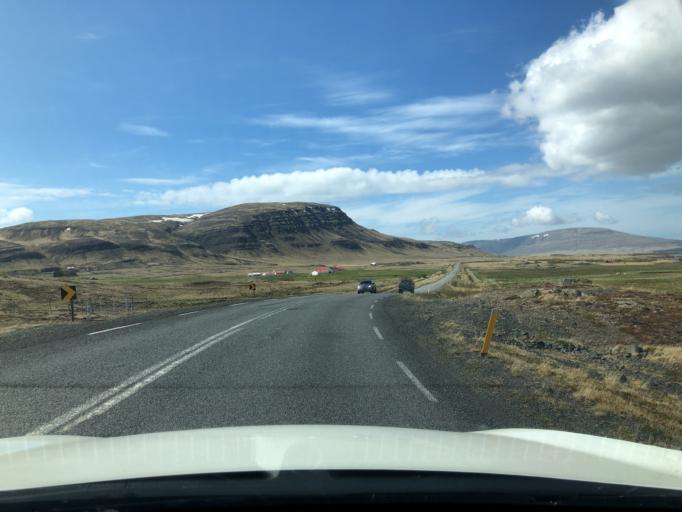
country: IS
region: Capital Region
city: Mosfellsbaer
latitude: 64.3303
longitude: -21.6352
